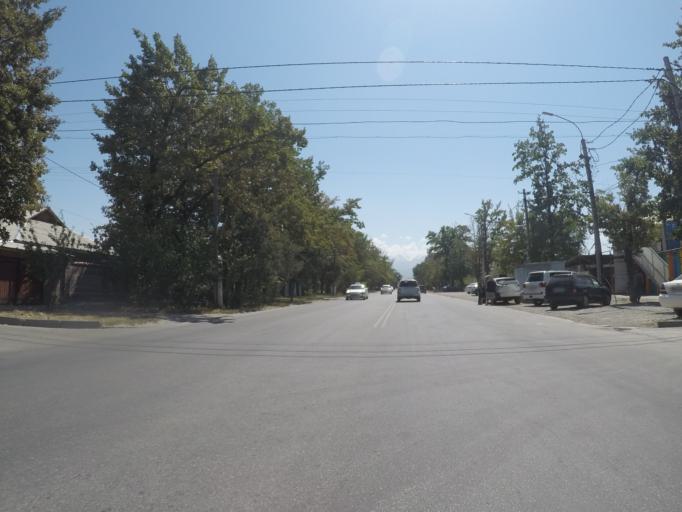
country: KG
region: Chuy
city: Bishkek
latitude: 42.8469
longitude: 74.5769
